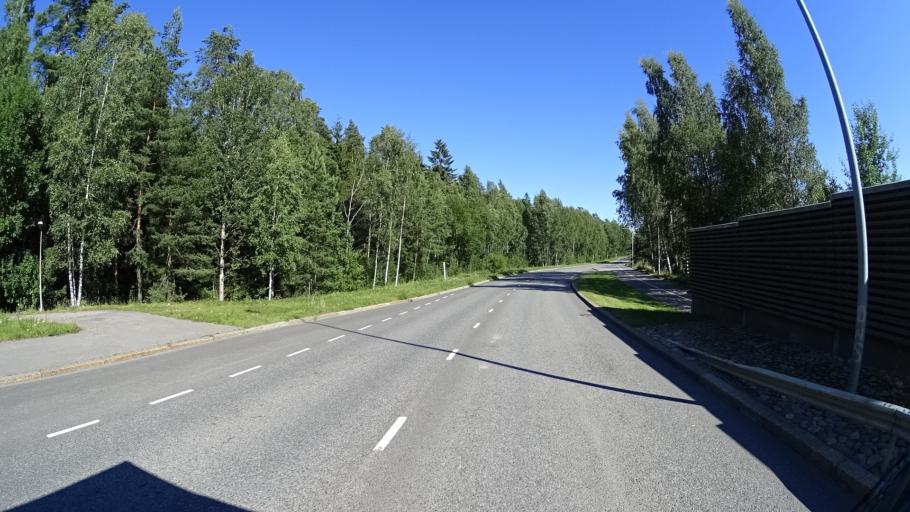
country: FI
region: Uusimaa
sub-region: Helsinki
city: Vantaa
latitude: 60.2239
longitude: 25.1451
